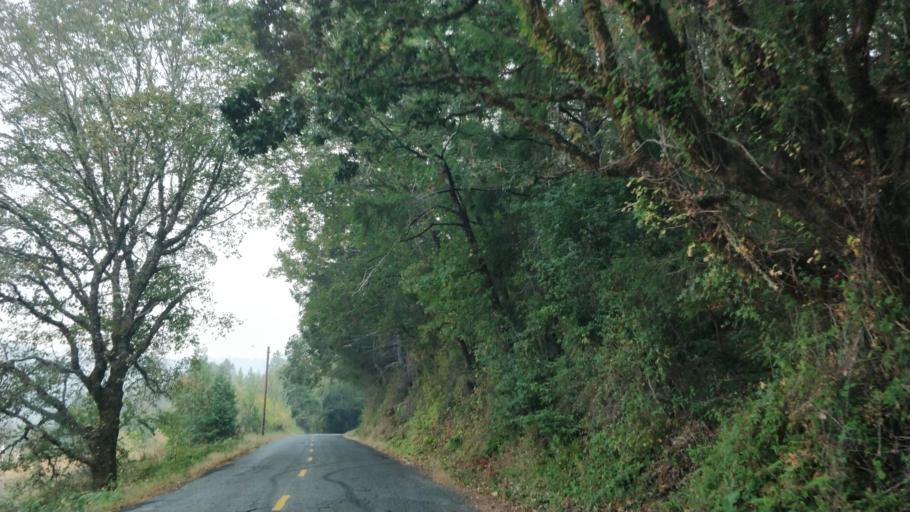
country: US
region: California
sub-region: Humboldt County
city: Rio Dell
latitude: 40.2378
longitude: -124.1607
